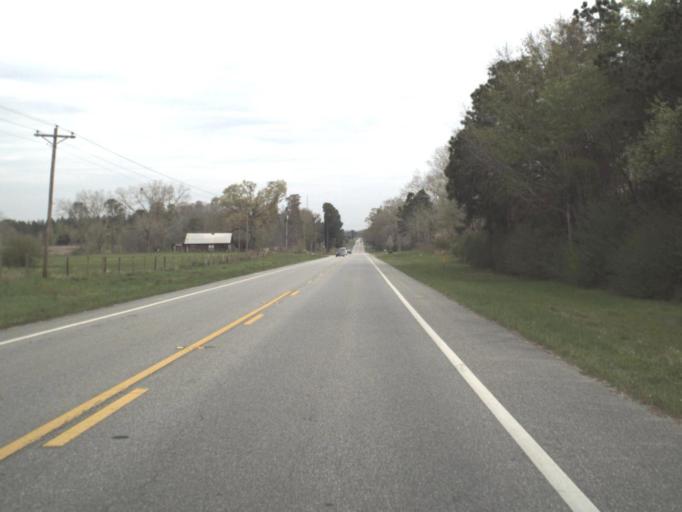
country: US
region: Florida
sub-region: Jackson County
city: Graceville
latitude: 30.9271
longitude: -85.6491
